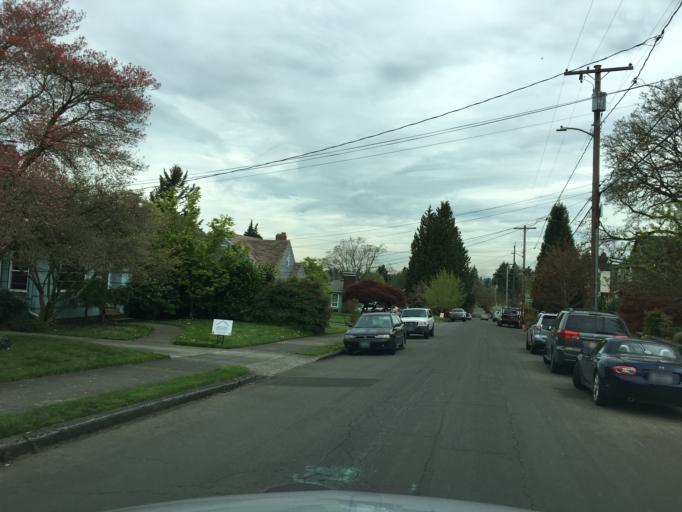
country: US
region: Oregon
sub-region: Multnomah County
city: Lents
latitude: 45.5214
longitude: -122.5996
